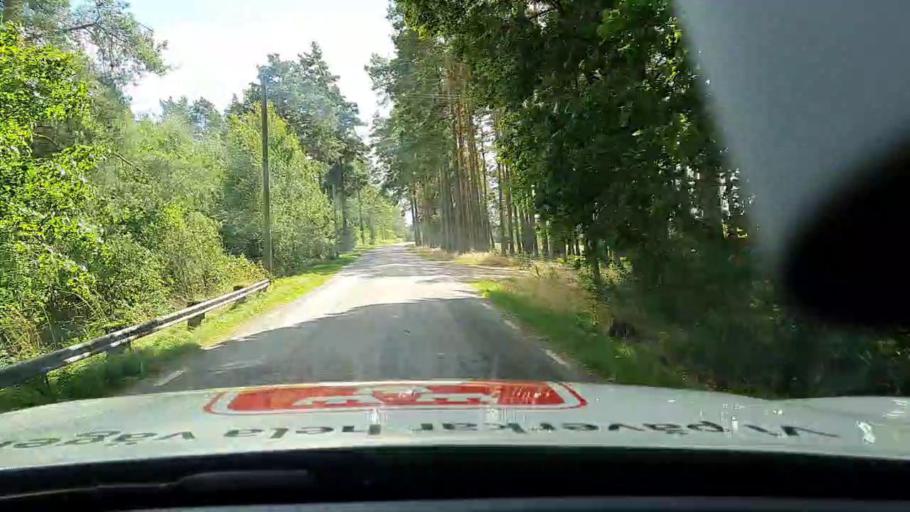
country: SE
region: Vaestra Goetaland
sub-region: Toreboda Kommun
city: Toereboda
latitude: 58.5763
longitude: 14.1238
